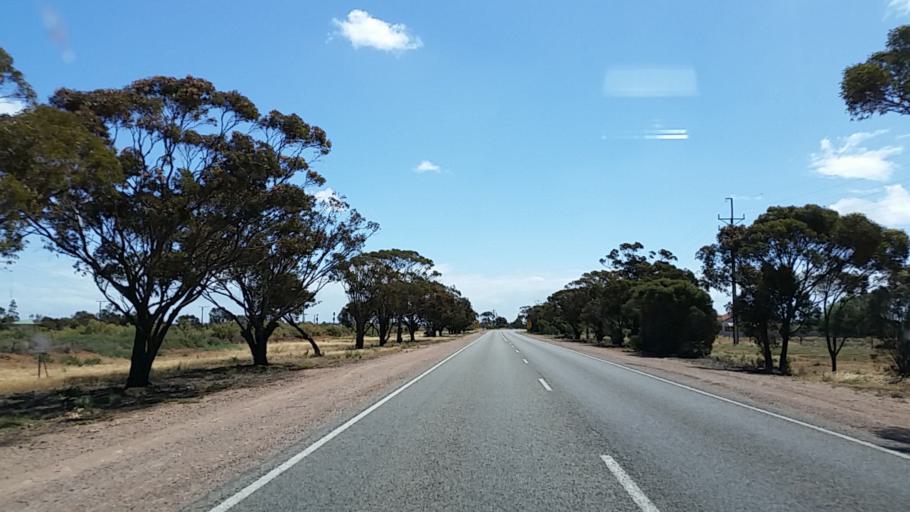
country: AU
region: South Australia
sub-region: Port Pirie City and Dists
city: Solomontown
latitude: -33.1941
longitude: 138.0482
